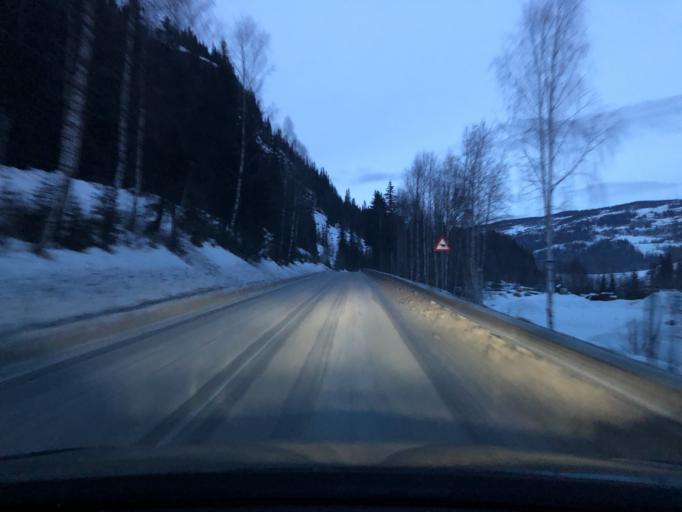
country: NO
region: Oppland
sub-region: Nord-Aurdal
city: Fagernes
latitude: 60.9993
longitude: 9.2103
